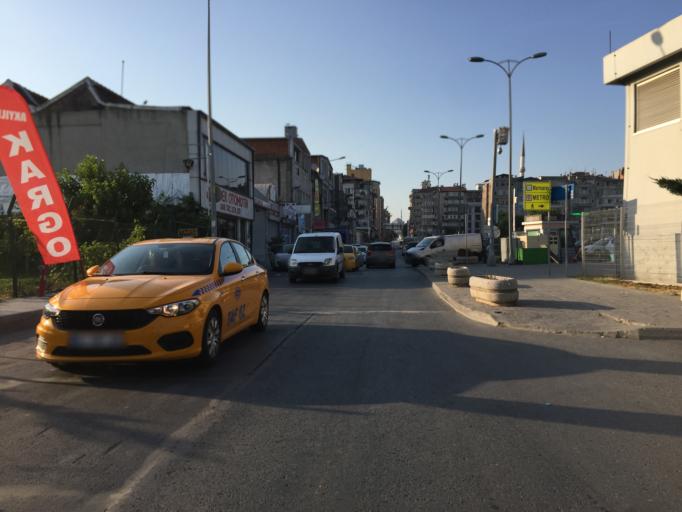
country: TR
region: Istanbul
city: Istanbul
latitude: 41.0048
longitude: 28.9502
